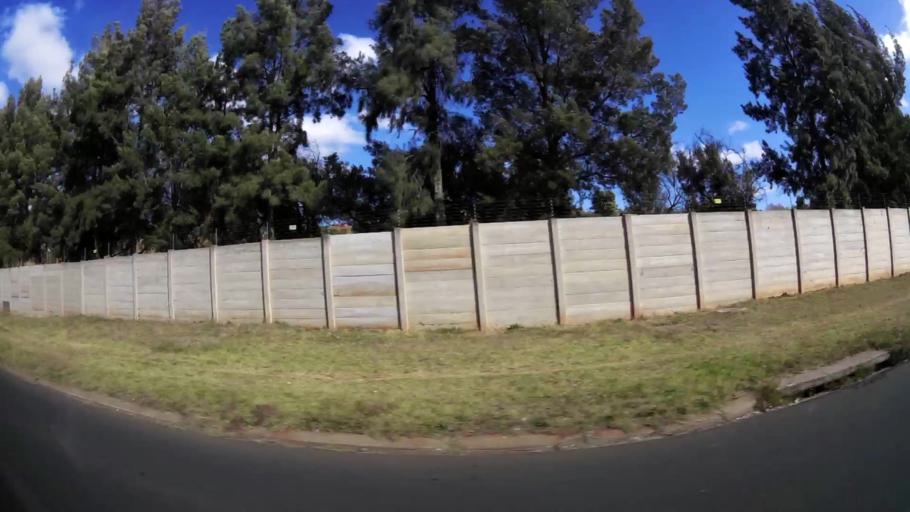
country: ZA
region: Gauteng
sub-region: West Rand District Municipality
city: Krugersdorp
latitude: -26.1047
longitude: 27.8388
